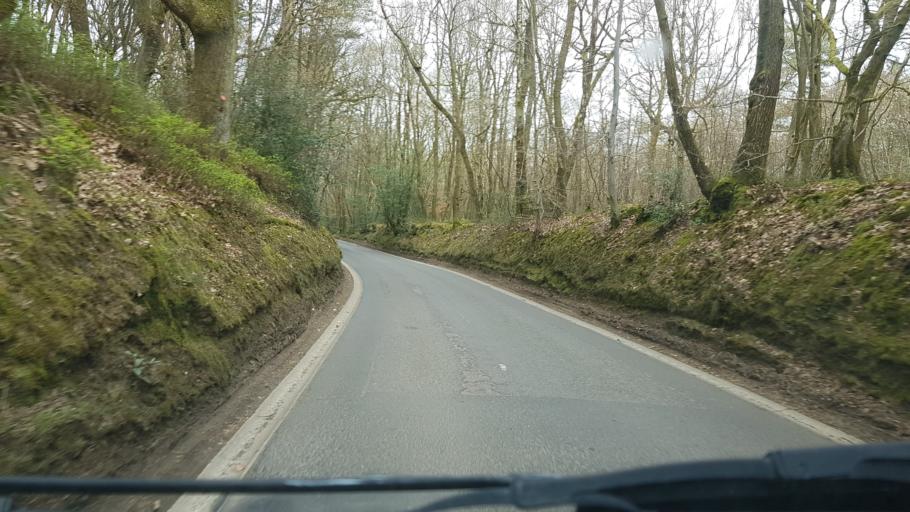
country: GB
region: England
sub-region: Surrey
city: Cranleigh
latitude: 51.1825
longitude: -0.4615
